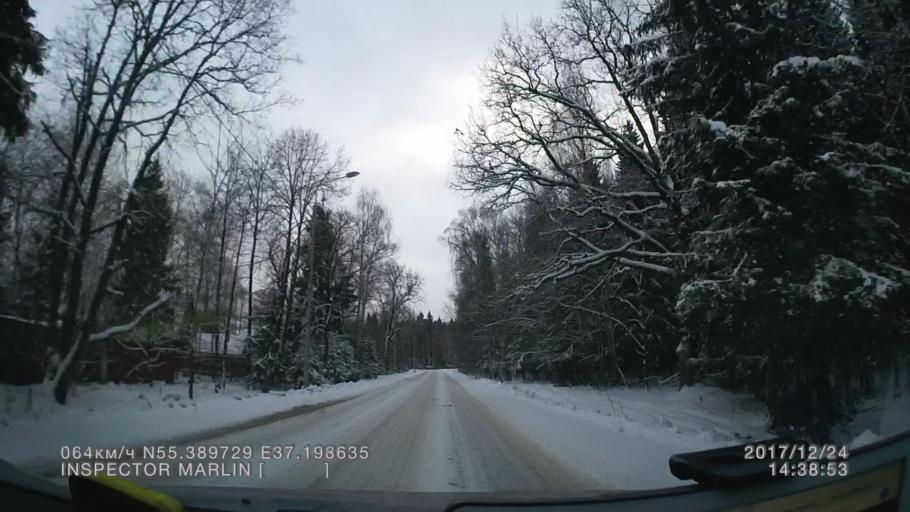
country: RU
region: Moskovskaya
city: Troitsk
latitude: 55.3895
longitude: 37.1988
